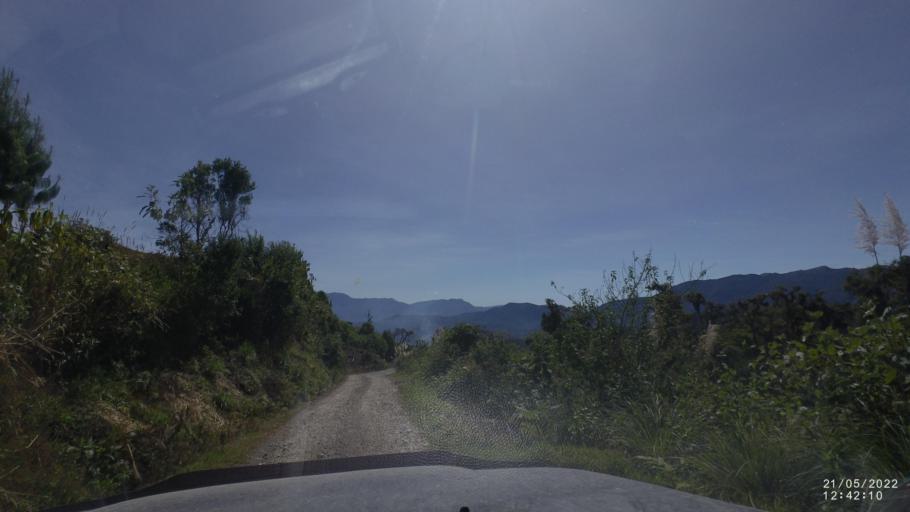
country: BO
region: Cochabamba
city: Colomi
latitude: -17.1933
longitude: -65.9290
